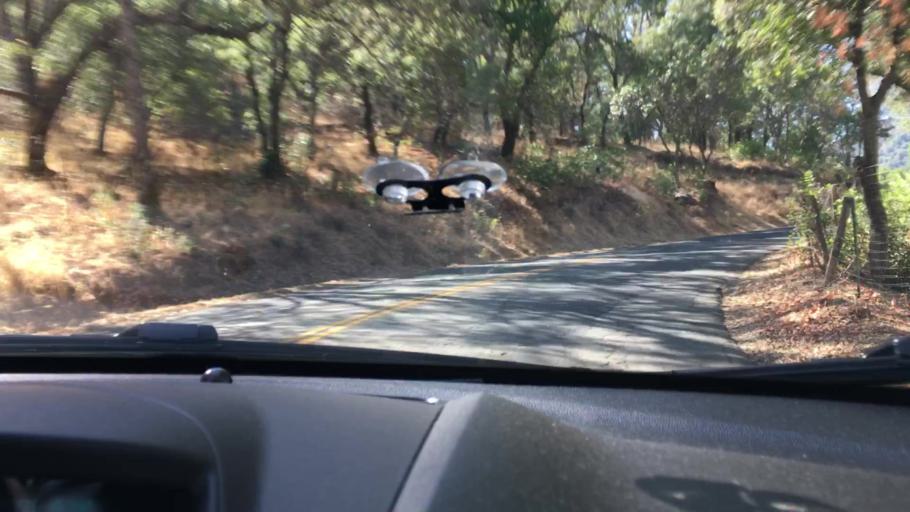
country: US
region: California
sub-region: Solano County
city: Green Valley
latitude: 38.3350
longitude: -122.1240
